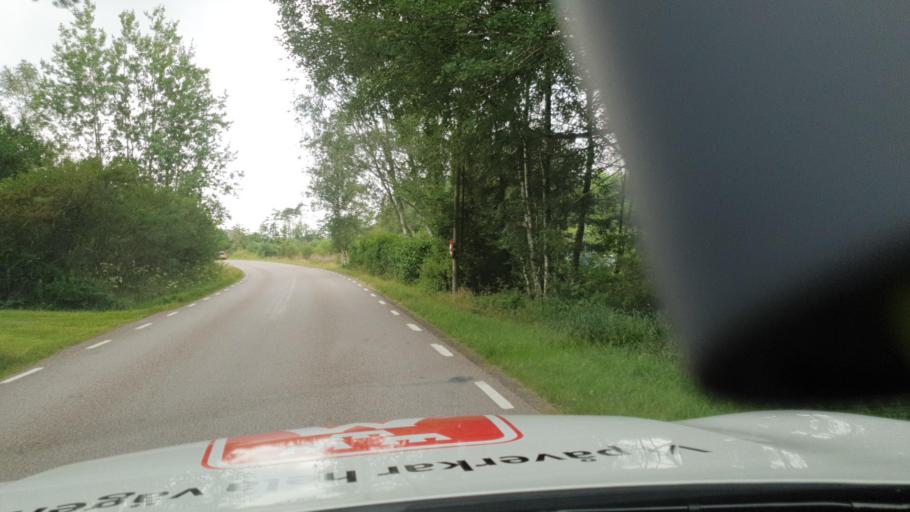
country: SE
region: Vaestra Goetaland
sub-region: Tanums Kommun
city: Grebbestad
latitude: 58.6332
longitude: 11.2828
